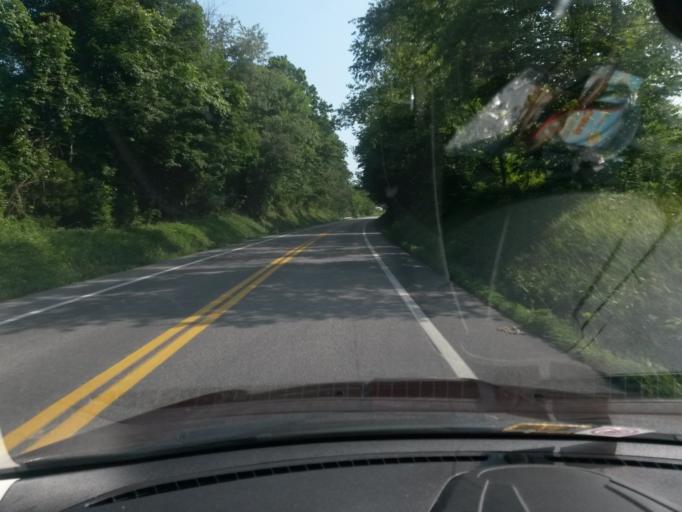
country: US
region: Virginia
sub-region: Shenandoah County
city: Basye
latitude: 38.7989
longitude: -78.8913
